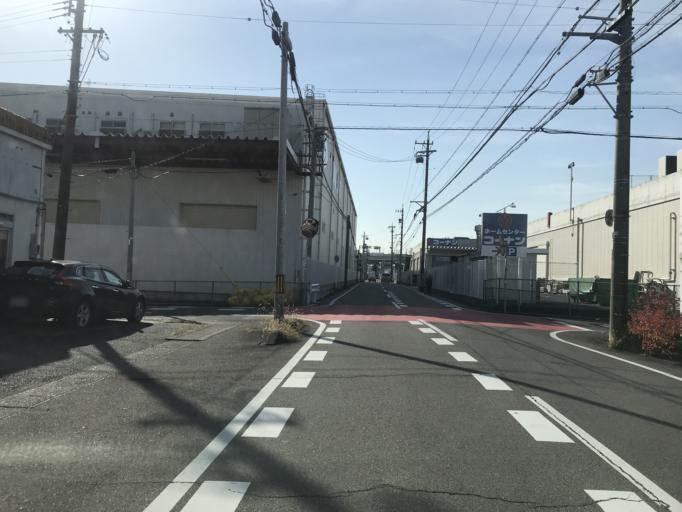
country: JP
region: Aichi
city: Iwakura
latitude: 35.2286
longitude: 136.8542
